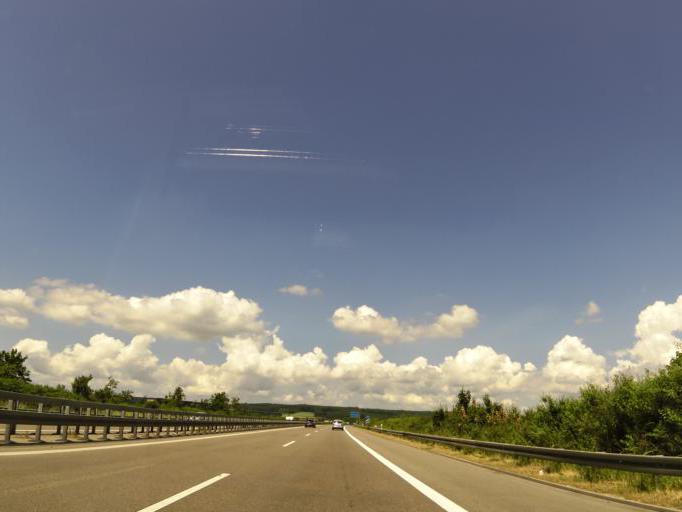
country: DE
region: Baden-Wuerttemberg
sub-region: Tuebingen Region
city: Langenau
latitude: 48.4868
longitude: 10.0950
